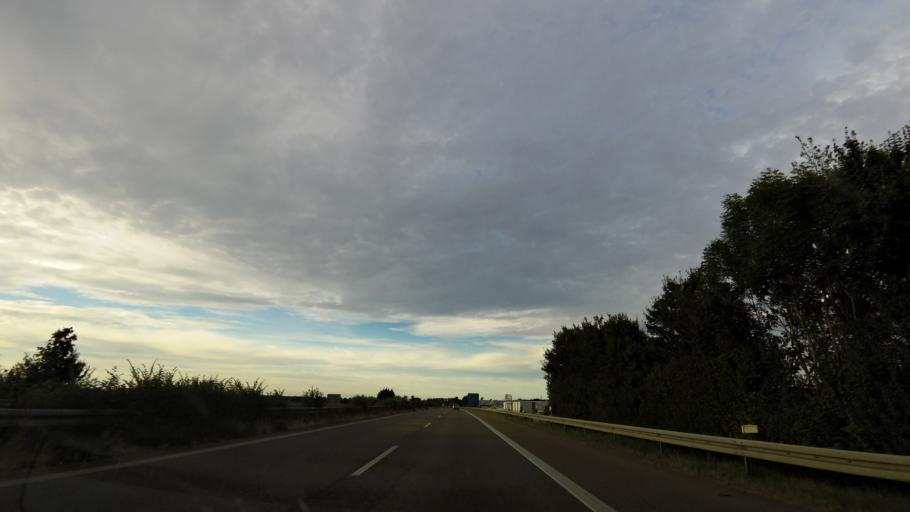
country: DE
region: Baden-Wuerttemberg
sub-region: Freiburg Region
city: Grafenhausen
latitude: 48.2716
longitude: 7.7764
